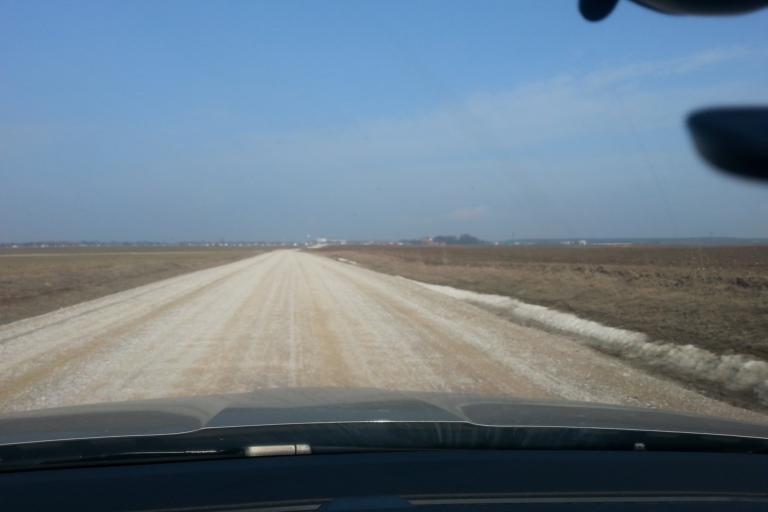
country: LT
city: Trakai
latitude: 54.5922
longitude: 24.9775
